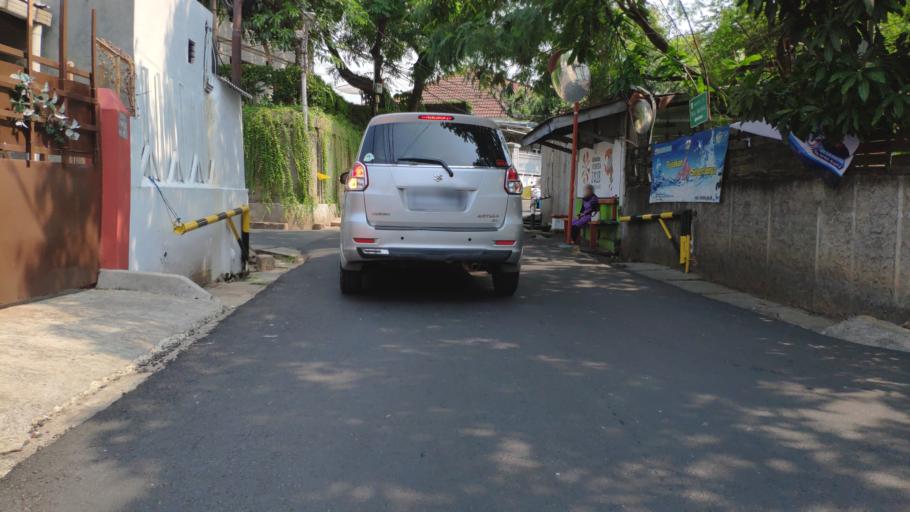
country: ID
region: Jakarta Raya
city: Jakarta
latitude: -6.2520
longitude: 106.8120
